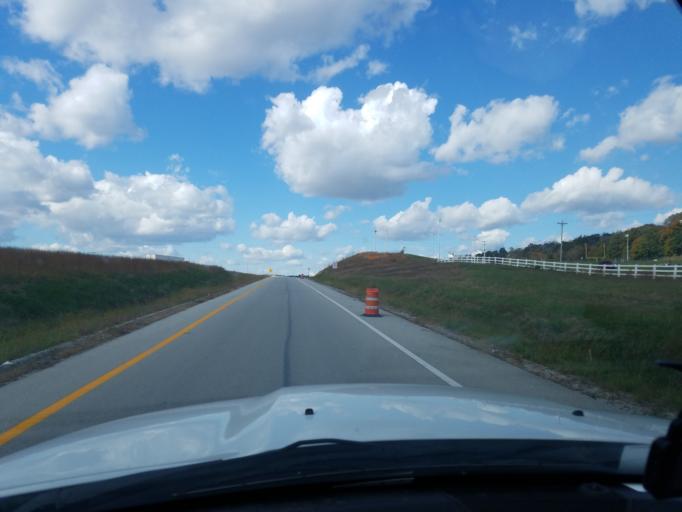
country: US
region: Kentucky
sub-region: Butler County
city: Morgantown
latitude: 37.2041
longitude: -86.7015
